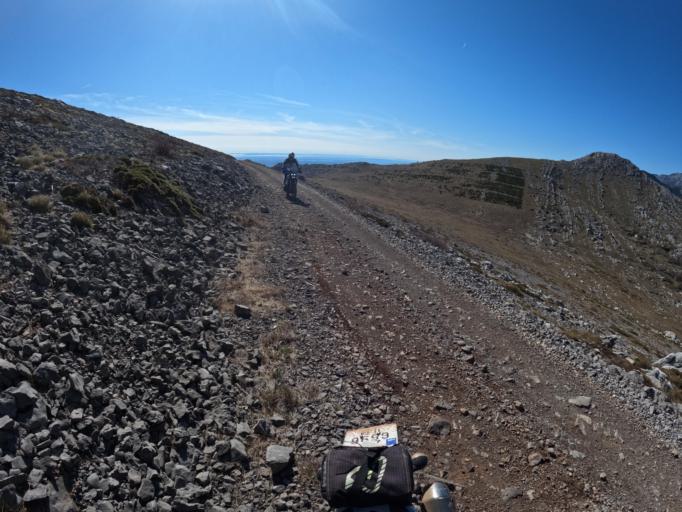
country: HR
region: Zadarska
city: Pridraga
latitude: 44.2872
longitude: 15.5795
